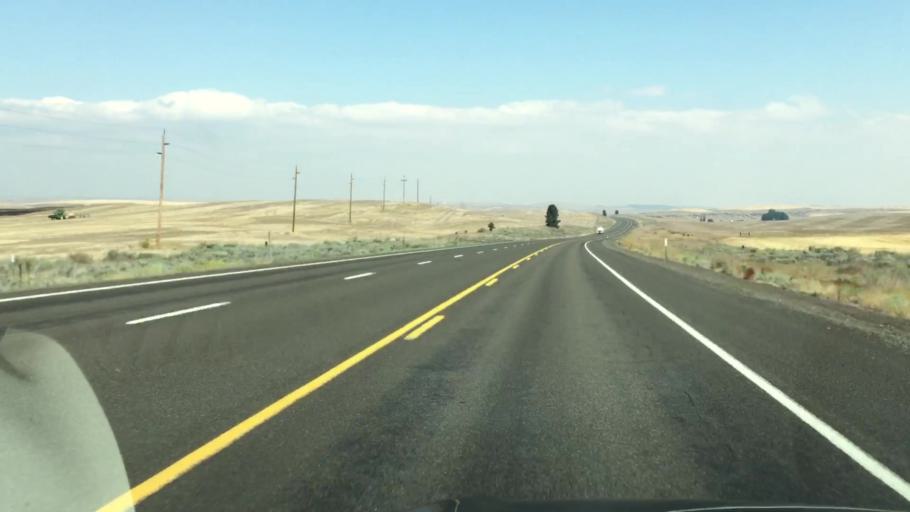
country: US
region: Oregon
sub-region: Wasco County
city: The Dalles
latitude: 45.3942
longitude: -121.1419
